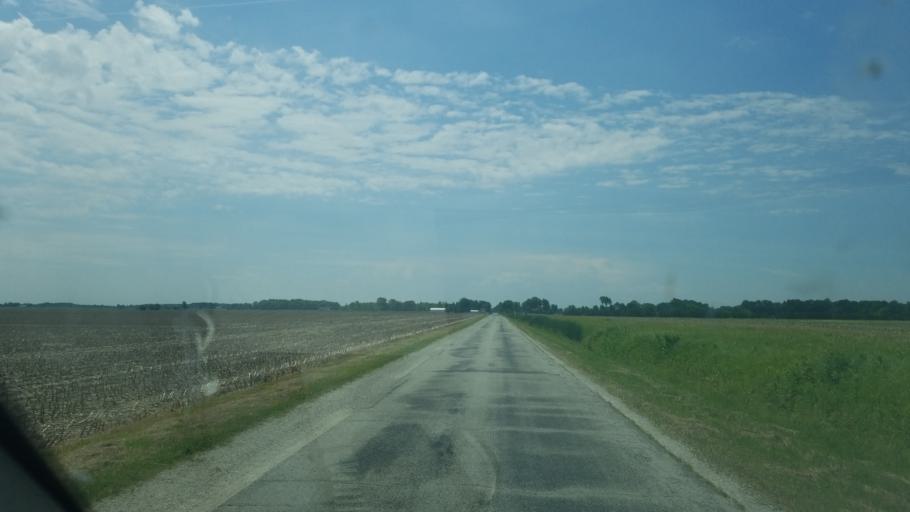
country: US
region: Ohio
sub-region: Wood County
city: North Baltimore
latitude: 41.2519
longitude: -83.6212
